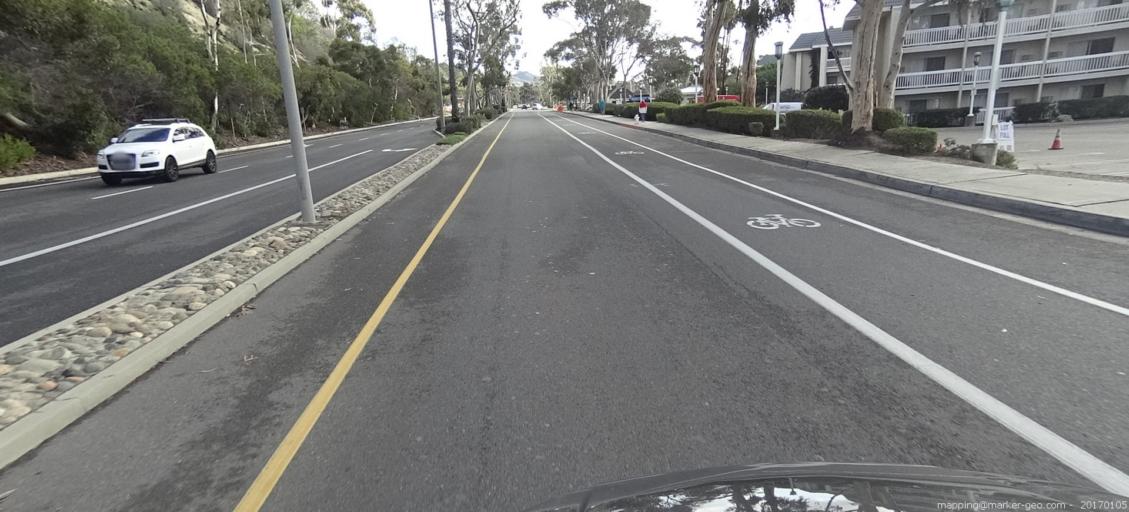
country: US
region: California
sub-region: Orange County
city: Dana Point
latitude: 33.4621
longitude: -117.6981
